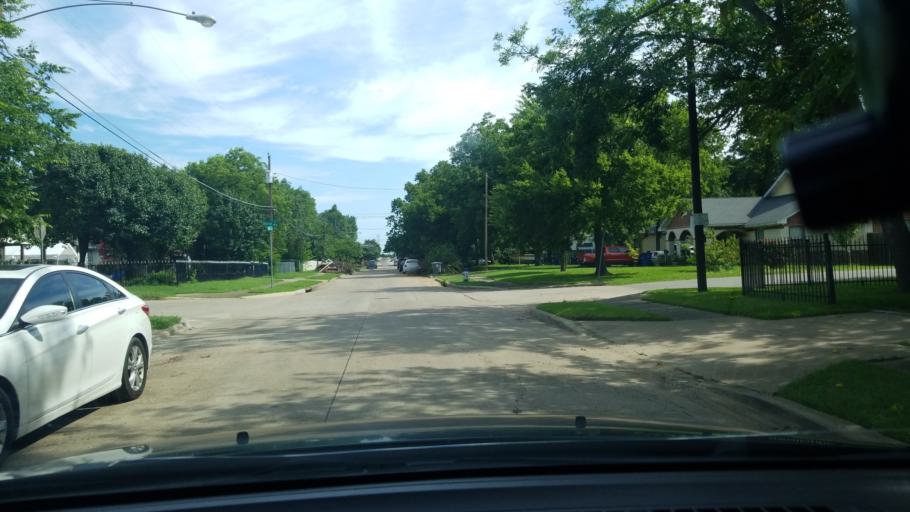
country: US
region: Texas
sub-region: Dallas County
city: Balch Springs
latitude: 32.7645
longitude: -96.6714
